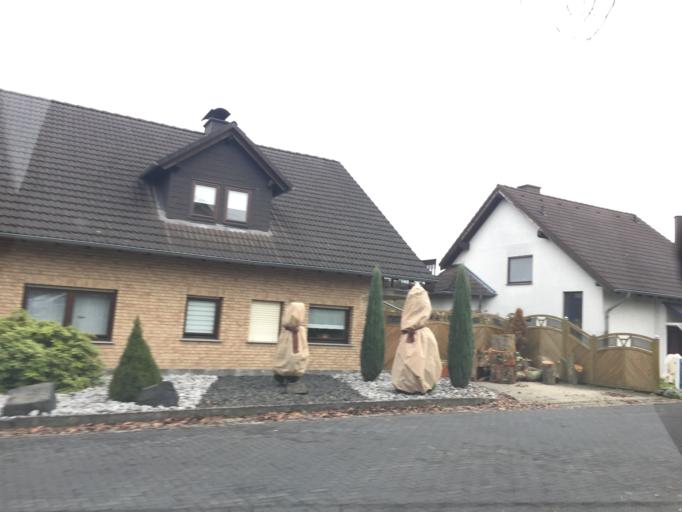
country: DE
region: Rheinland-Pfalz
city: Heiligenroth
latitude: 50.4459
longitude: 7.8662
